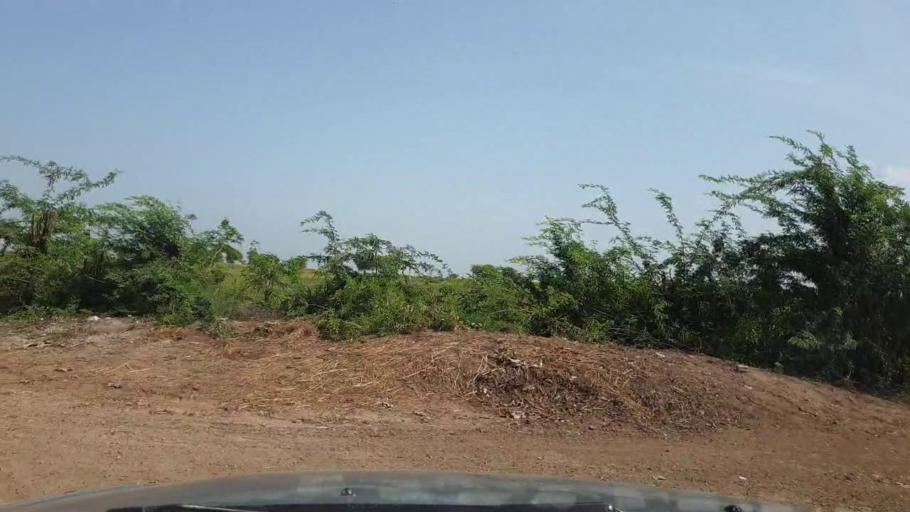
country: PK
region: Sindh
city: Rajo Khanani
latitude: 25.0159
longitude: 68.8000
